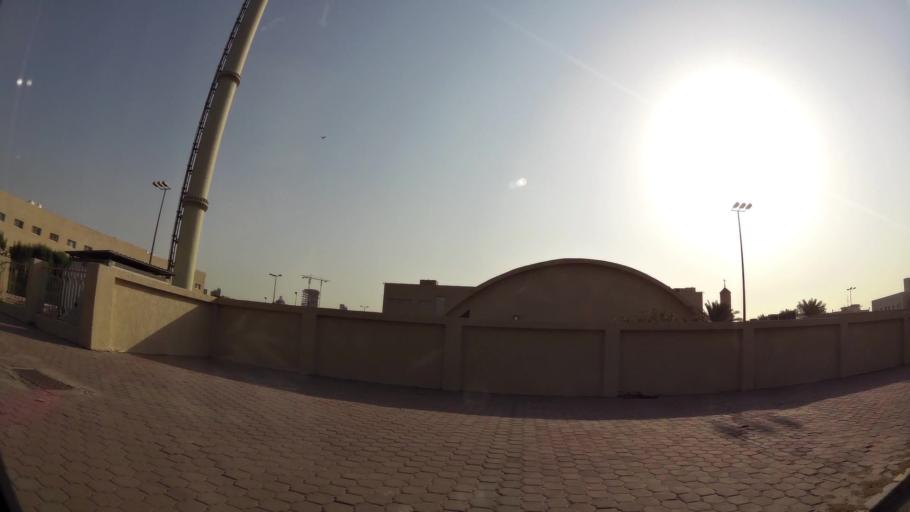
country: KW
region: Al Asimah
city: Ad Dasmah
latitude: 29.3637
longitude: 48.0013
